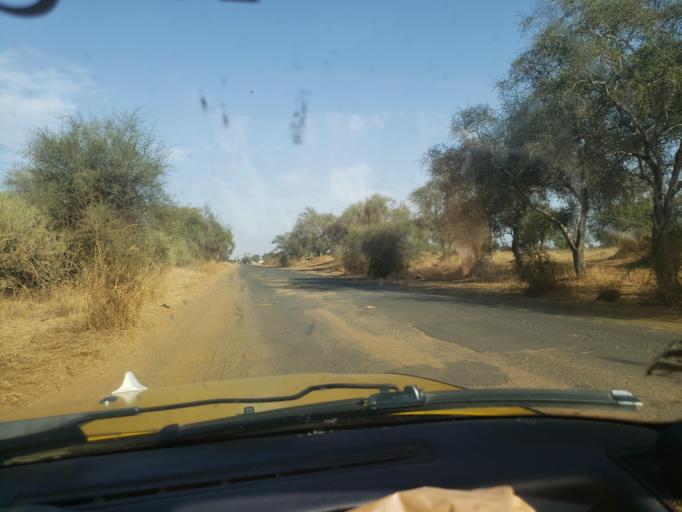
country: SN
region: Louga
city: Louga
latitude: 15.5123
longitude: -16.0026
